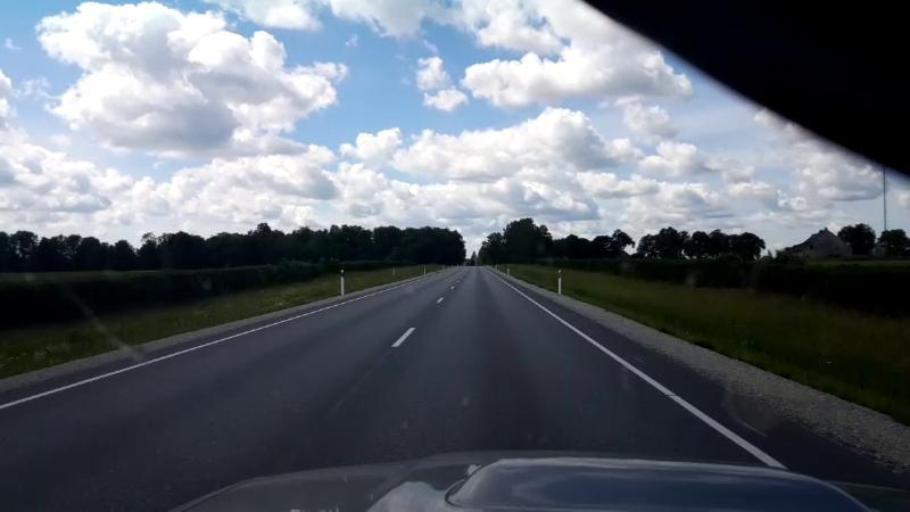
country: EE
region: Jaervamaa
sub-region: Jaerva-Jaani vald
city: Jarva-Jaani
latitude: 59.1013
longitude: 25.7056
